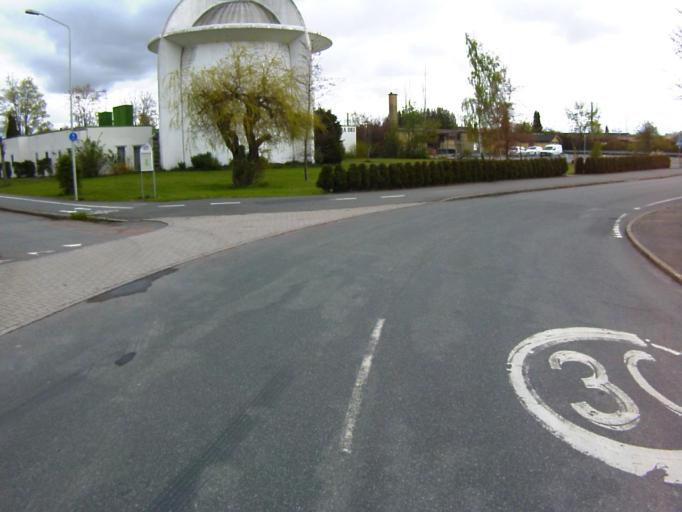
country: SE
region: Skane
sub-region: Kristianstads Kommun
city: Kristianstad
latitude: 56.0513
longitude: 14.1760
